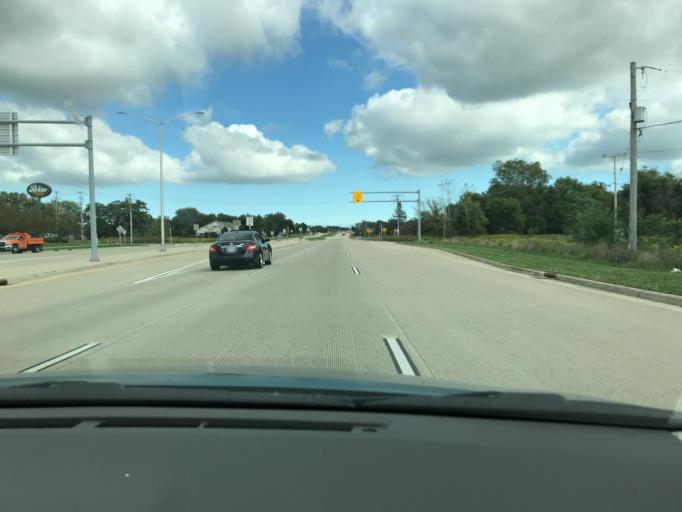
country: US
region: Wisconsin
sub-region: Kenosha County
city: Pleasant Prairie
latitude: 42.5673
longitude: -87.9490
